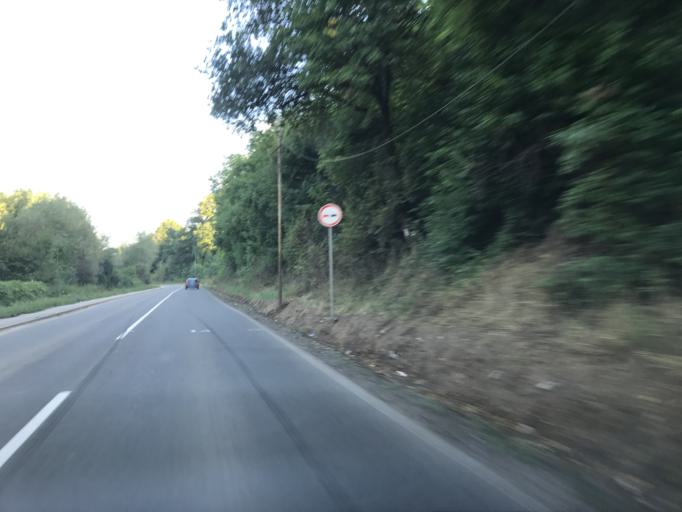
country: RS
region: Central Serbia
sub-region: Belgrade
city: Grocka
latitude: 44.6705
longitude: 20.7225
